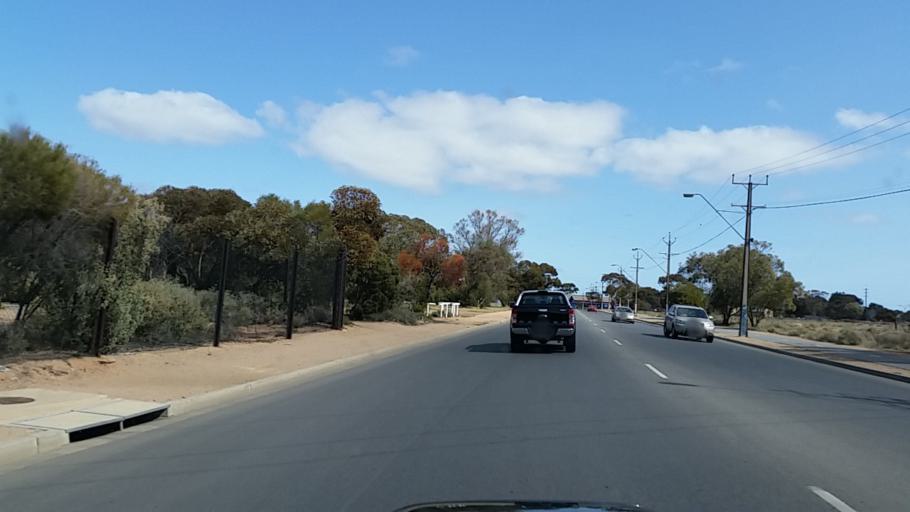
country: AU
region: South Australia
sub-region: Port Pirie City and Dists
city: Port Pirie
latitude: -33.1872
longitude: 138.0117
